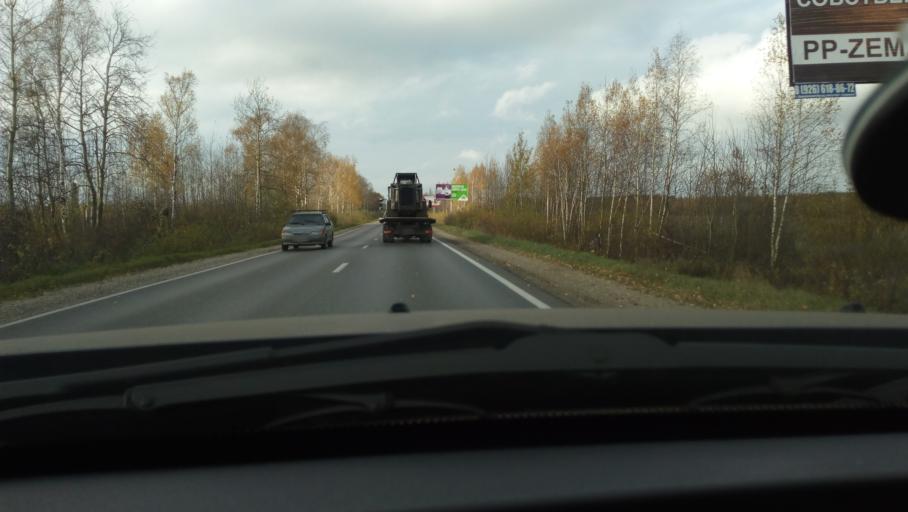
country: RU
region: Moskovskaya
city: Rakhmanovo
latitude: 55.7506
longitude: 38.6191
